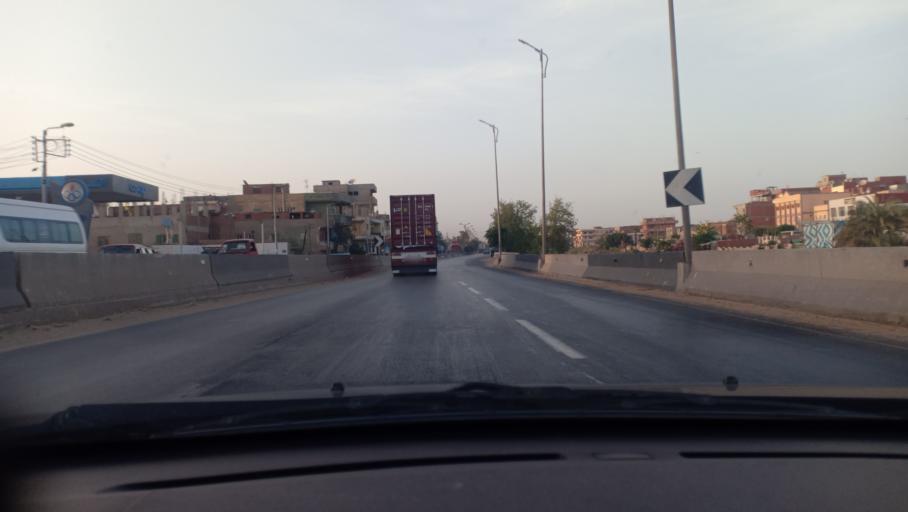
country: EG
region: Muhafazat al Gharbiyah
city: Zifta
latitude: 30.6402
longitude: 31.2814
